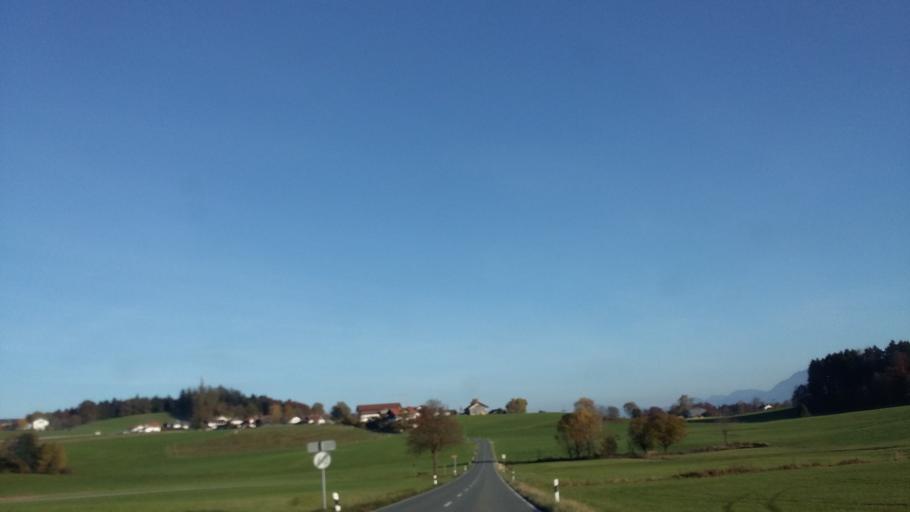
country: DE
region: Bavaria
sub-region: Upper Bavaria
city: Prien am Chiemsee
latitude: 47.8583
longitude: 12.3201
